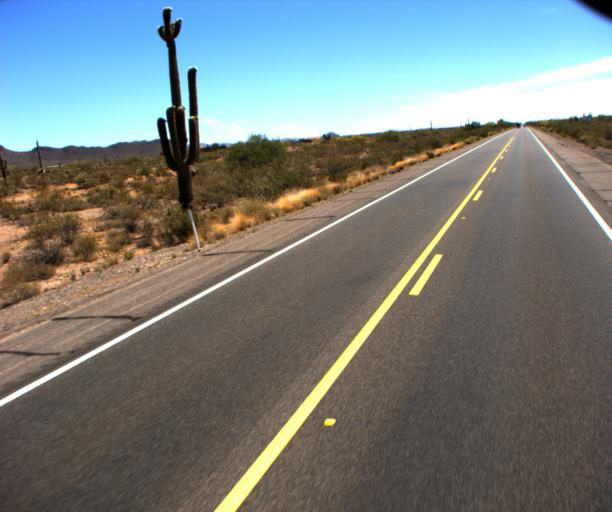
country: US
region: Arizona
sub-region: Maricopa County
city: Wickenburg
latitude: 33.8616
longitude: -112.6105
